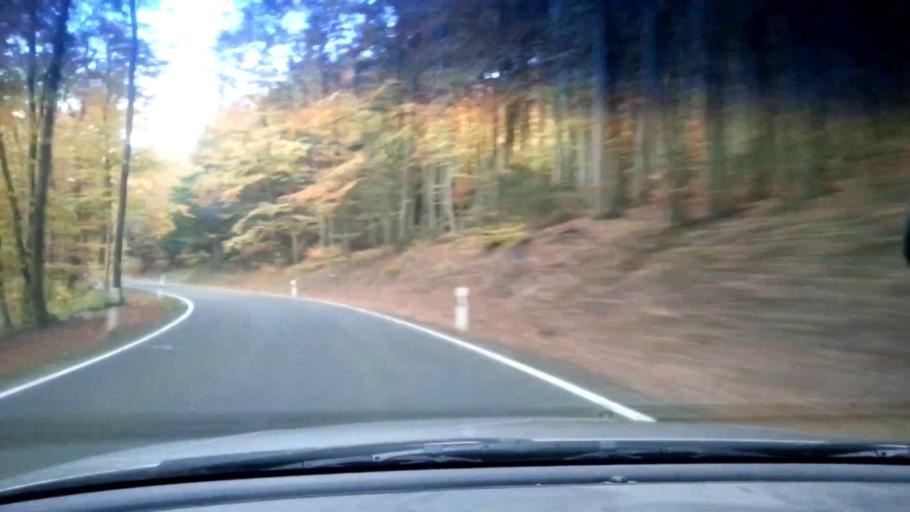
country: DE
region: Bavaria
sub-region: Upper Franconia
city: Heiligenstadt
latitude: 49.8664
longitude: 11.1281
